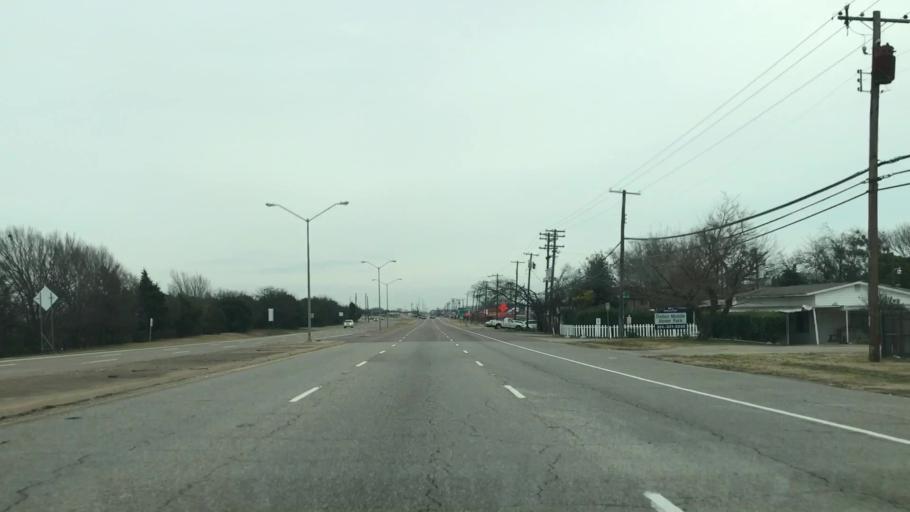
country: US
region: Texas
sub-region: Dallas County
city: Cockrell Hill
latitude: 32.7496
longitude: -96.8860
